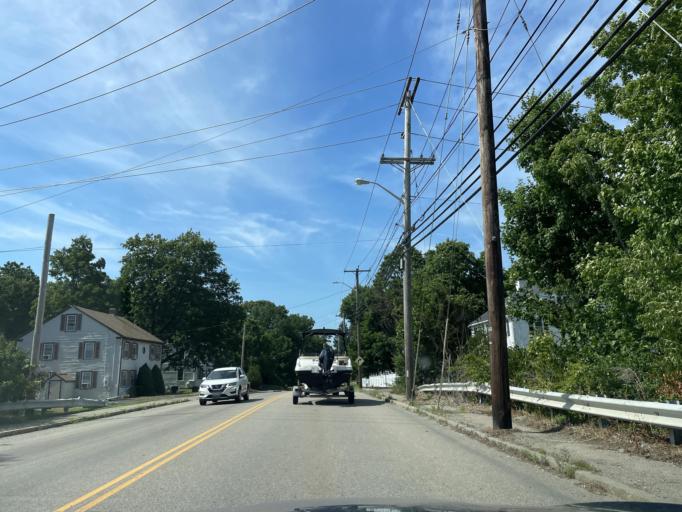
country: US
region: Massachusetts
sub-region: Norfolk County
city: Wrentham
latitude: 42.0683
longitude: -71.3290
